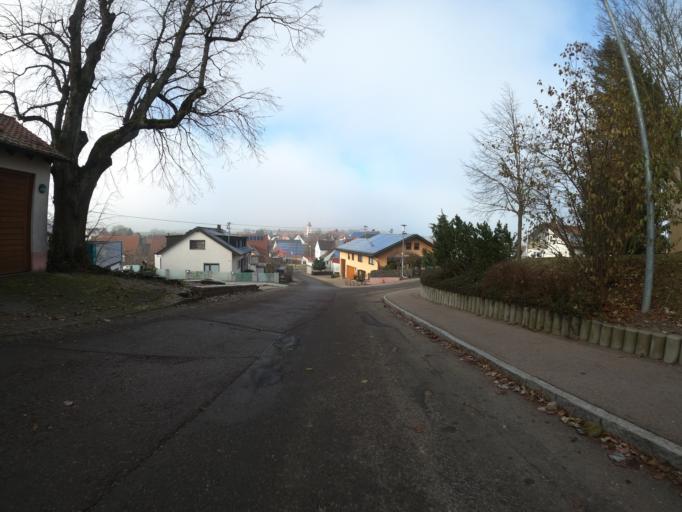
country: DE
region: Baden-Wuerttemberg
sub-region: Regierungsbezirk Stuttgart
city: Bad Uberkingen
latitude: 48.5850
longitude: 9.7668
